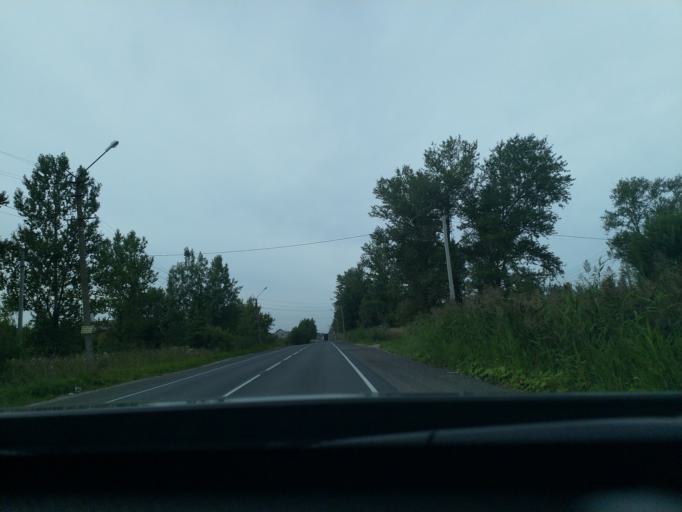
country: RU
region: Leningrad
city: Nikol'skoye
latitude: 59.7125
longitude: 30.7797
